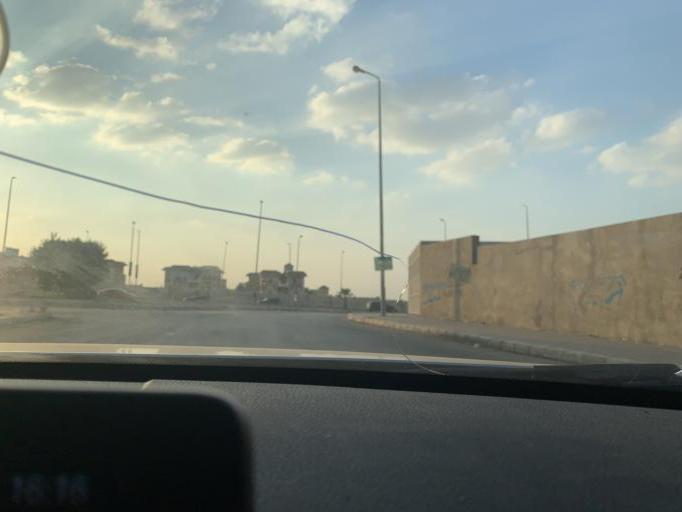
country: EG
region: Muhafazat al Qalyubiyah
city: Al Khankah
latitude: 30.0188
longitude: 31.4757
